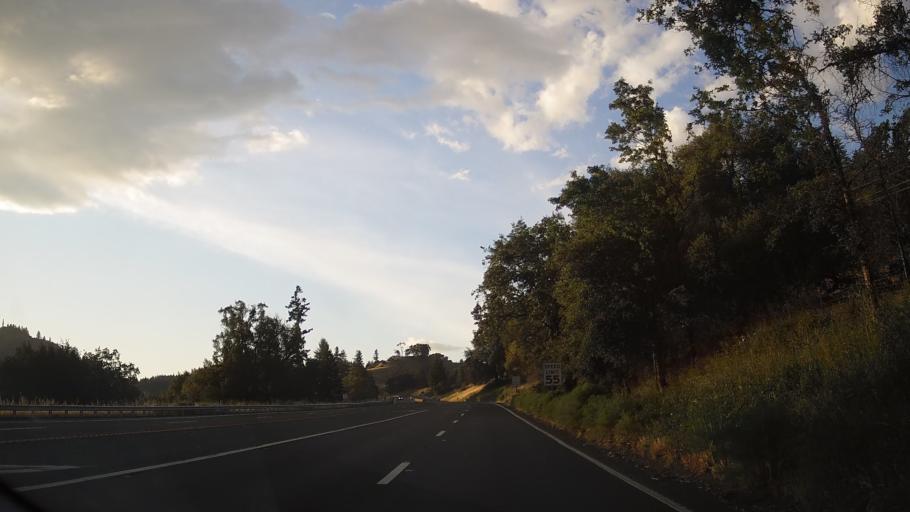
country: US
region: California
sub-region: Mendocino County
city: Willits
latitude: 39.3245
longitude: -123.3012
